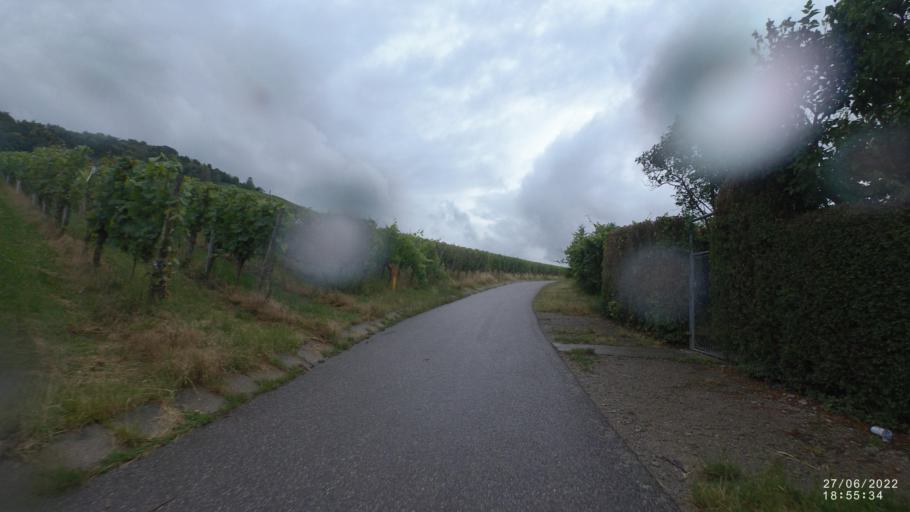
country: DE
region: Baden-Wuerttemberg
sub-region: Regierungsbezirk Stuttgart
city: Fellbach
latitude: 48.8012
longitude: 9.2787
